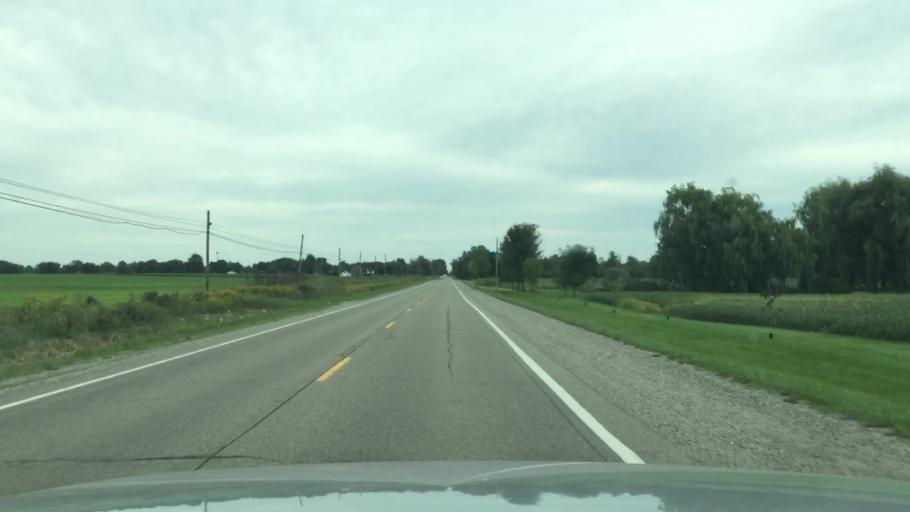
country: US
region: Michigan
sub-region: Genesee County
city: Swartz Creek
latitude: 42.9570
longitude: -83.8833
